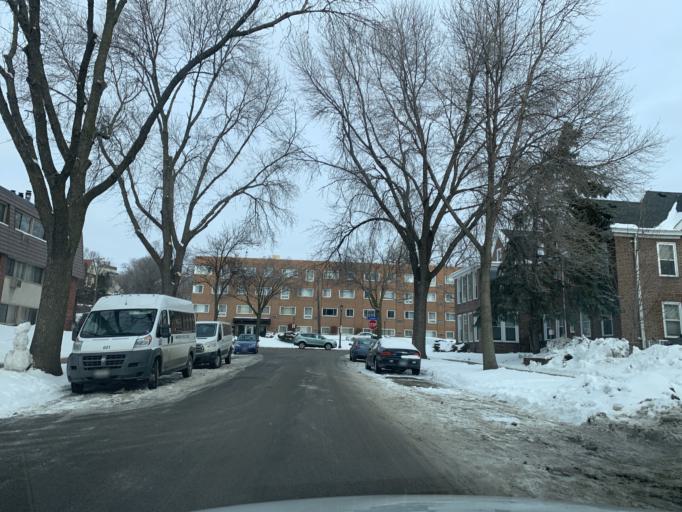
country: US
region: Minnesota
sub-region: Hennepin County
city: Minneapolis
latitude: 44.9622
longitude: -93.2829
